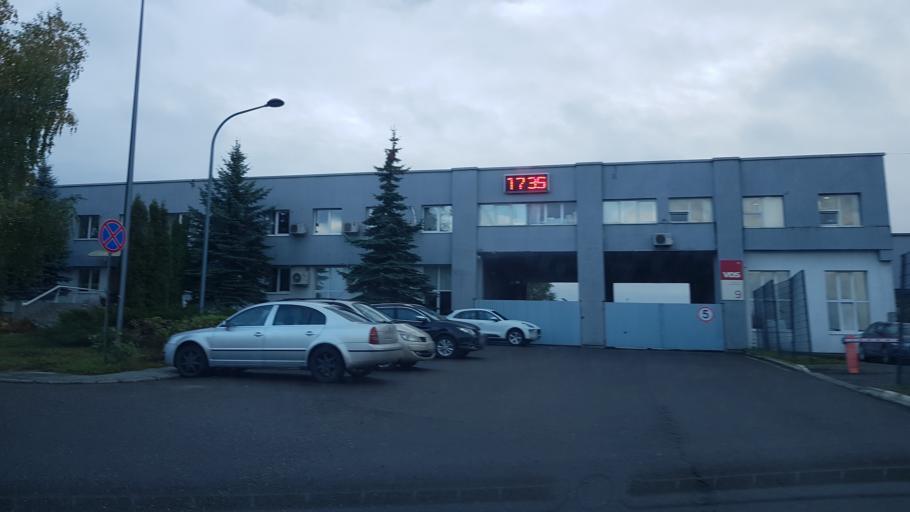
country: BY
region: Minsk
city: Malinovka
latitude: 53.8766
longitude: 27.4100
